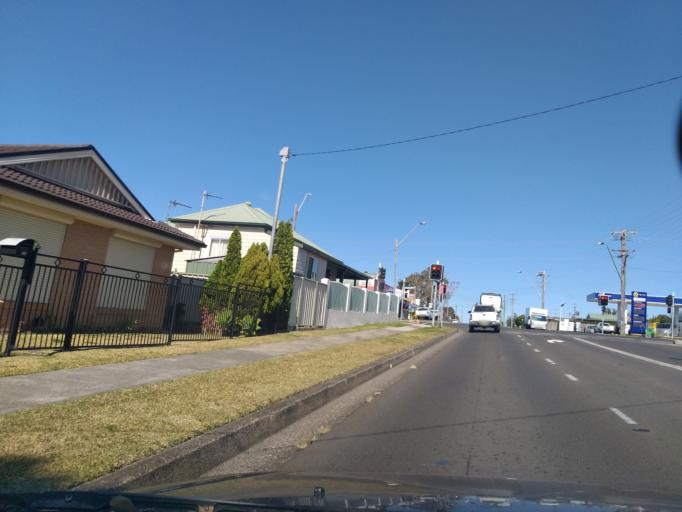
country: AU
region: New South Wales
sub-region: Wollongong
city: East Corrimal
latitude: -34.3677
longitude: 150.9105
